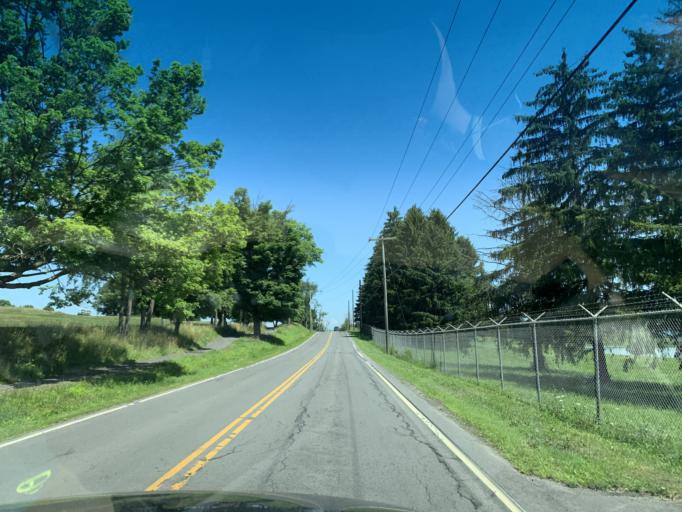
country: US
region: New York
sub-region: Oneida County
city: Utica
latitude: 43.0748
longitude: -75.2369
